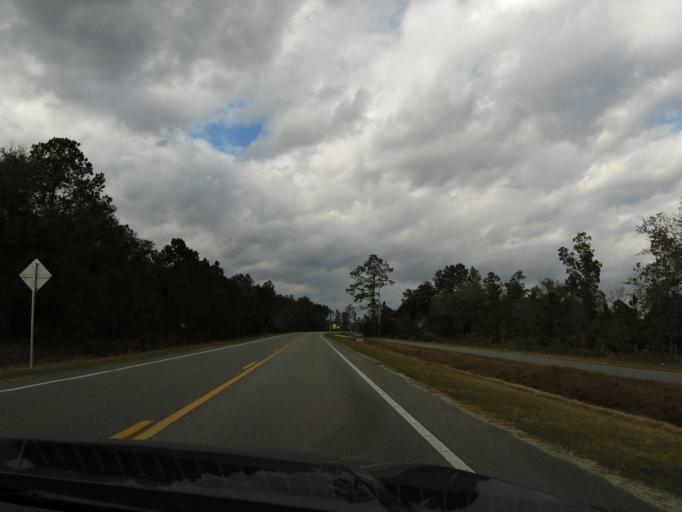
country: US
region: Florida
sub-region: Volusia County
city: Pierson
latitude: 29.2529
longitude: -81.4674
